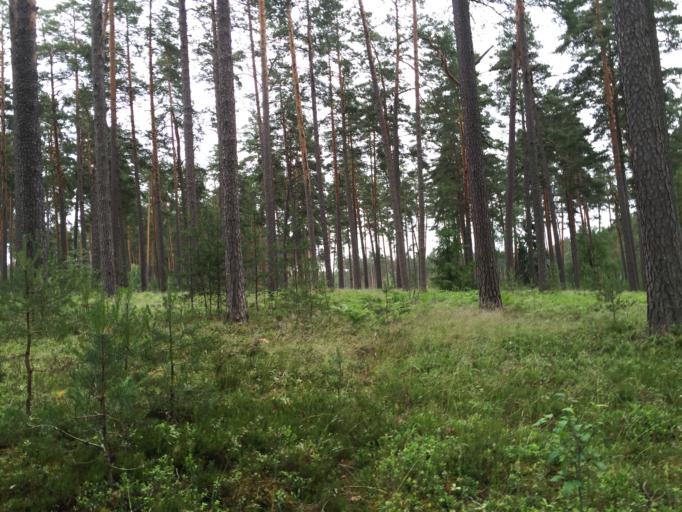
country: LV
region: Riga
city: Jaunciems
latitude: 57.0407
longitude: 24.2361
